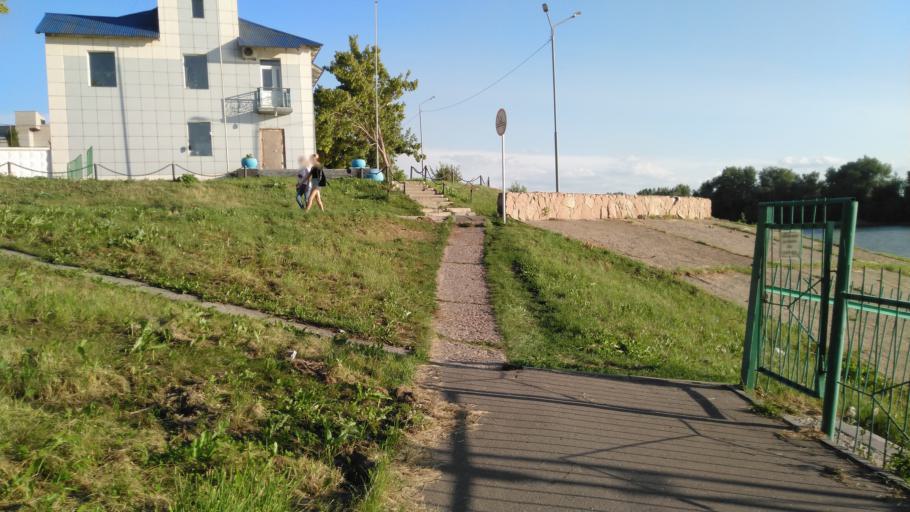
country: KZ
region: Pavlodar
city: Pavlodar
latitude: 52.2782
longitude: 76.9334
